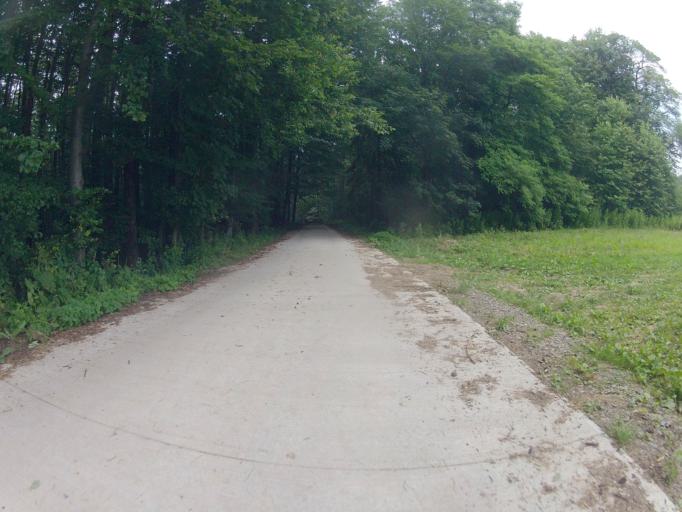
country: PL
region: Lesser Poland Voivodeship
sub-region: Powiat nowosadecki
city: Stary Sacz
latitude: 49.5627
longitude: 20.6252
